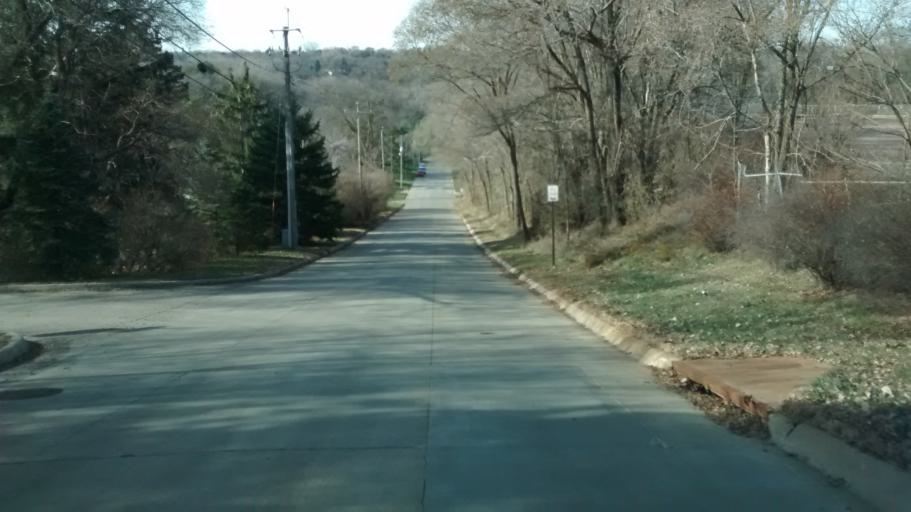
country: US
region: Iowa
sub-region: Woodbury County
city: Sioux City
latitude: 42.5375
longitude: -96.4037
